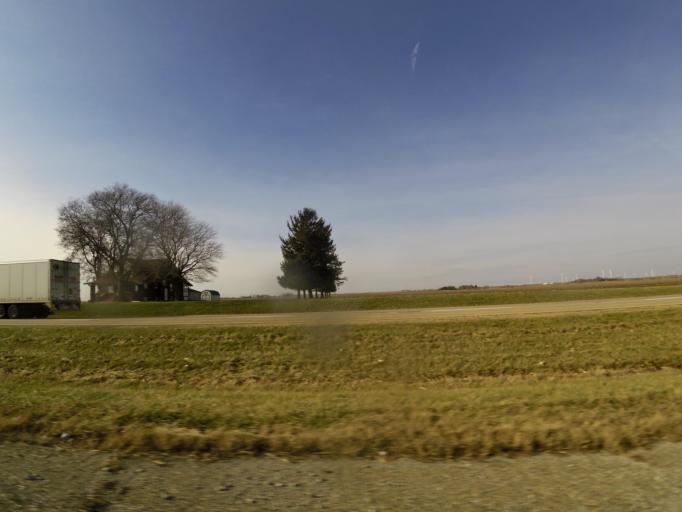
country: US
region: Illinois
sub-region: Macon County
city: Forsyth
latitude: 39.9473
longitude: -88.9554
